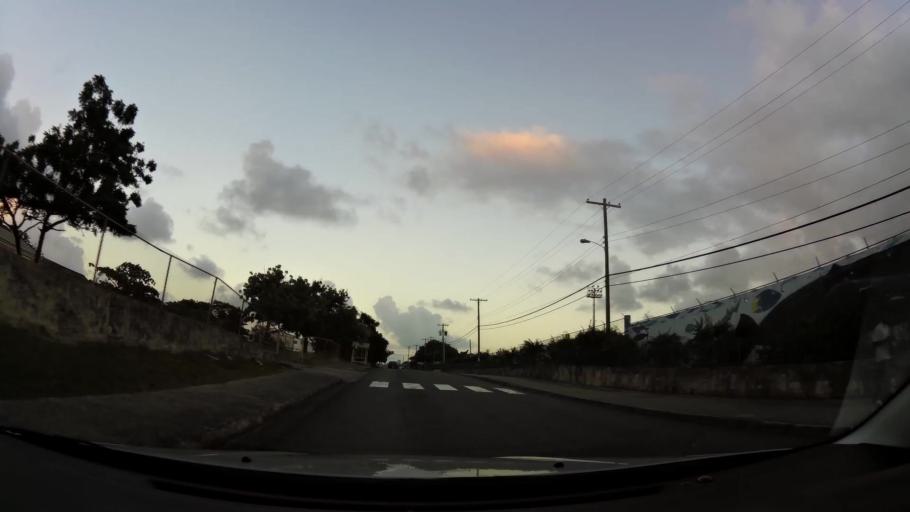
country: AG
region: Saint John
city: Saint John's
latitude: 17.1240
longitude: -61.8337
